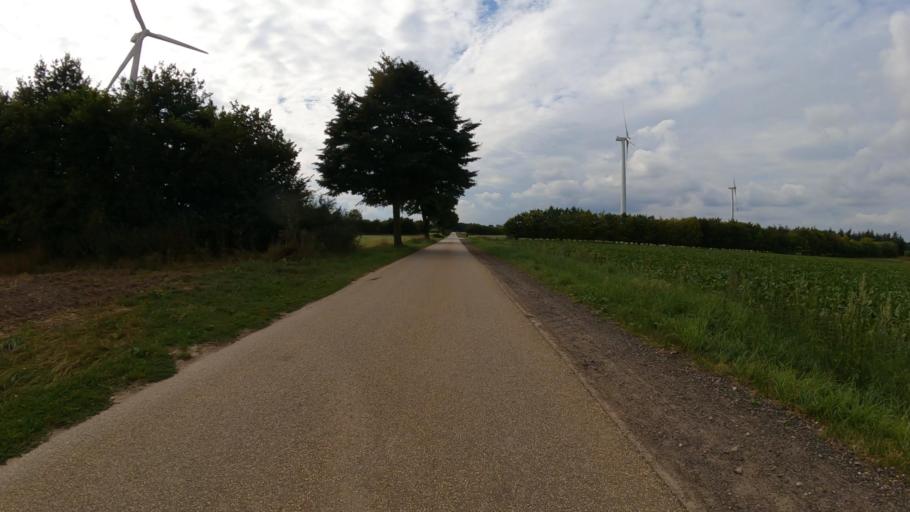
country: DE
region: Lower Saxony
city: Appel
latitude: 53.3905
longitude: 9.7754
